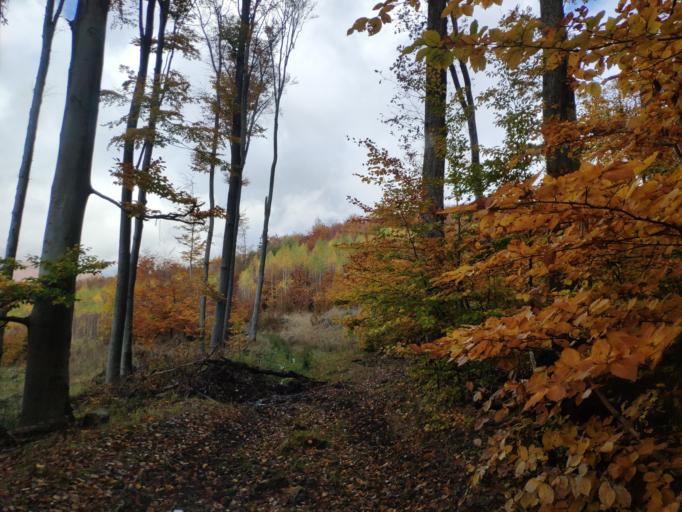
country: SK
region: Kosicky
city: Medzev
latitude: 48.7362
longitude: 20.9873
